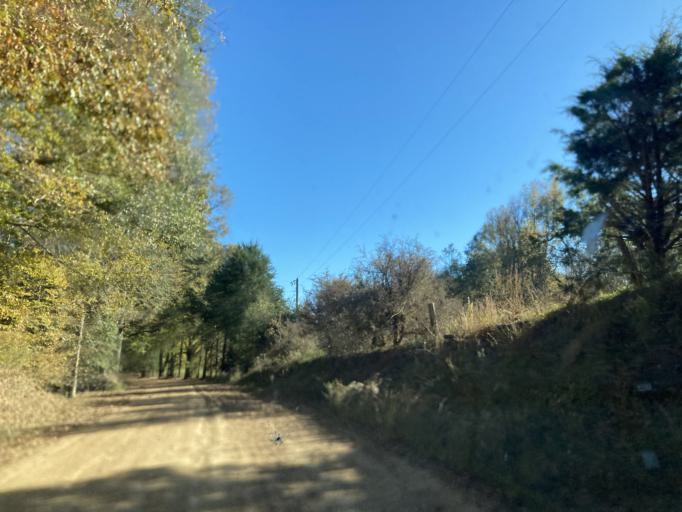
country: US
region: Mississippi
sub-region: Yazoo County
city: Yazoo City
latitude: 32.7385
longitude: -90.4393
